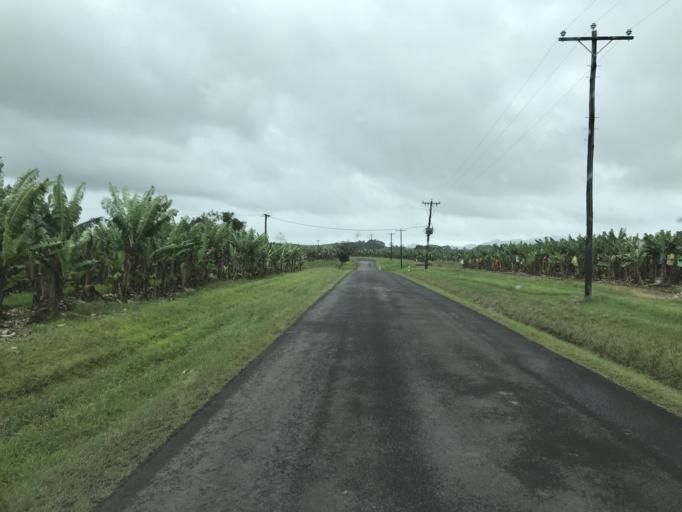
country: AU
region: Queensland
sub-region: Cassowary Coast
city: Innisfail
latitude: -17.5130
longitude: 145.9788
